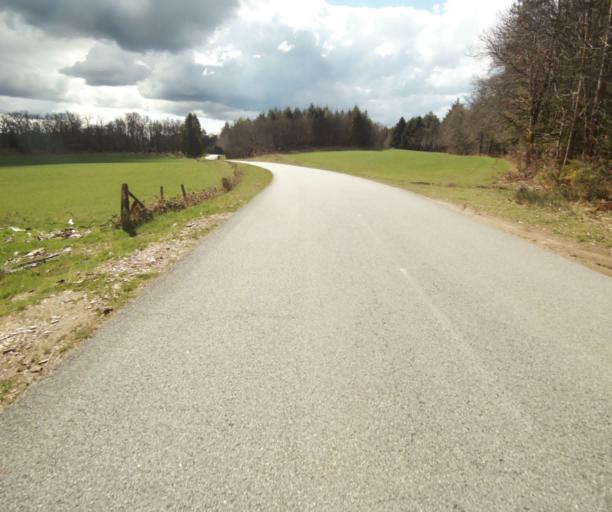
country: FR
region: Limousin
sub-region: Departement de la Correze
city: Correze
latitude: 45.2934
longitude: 1.8963
